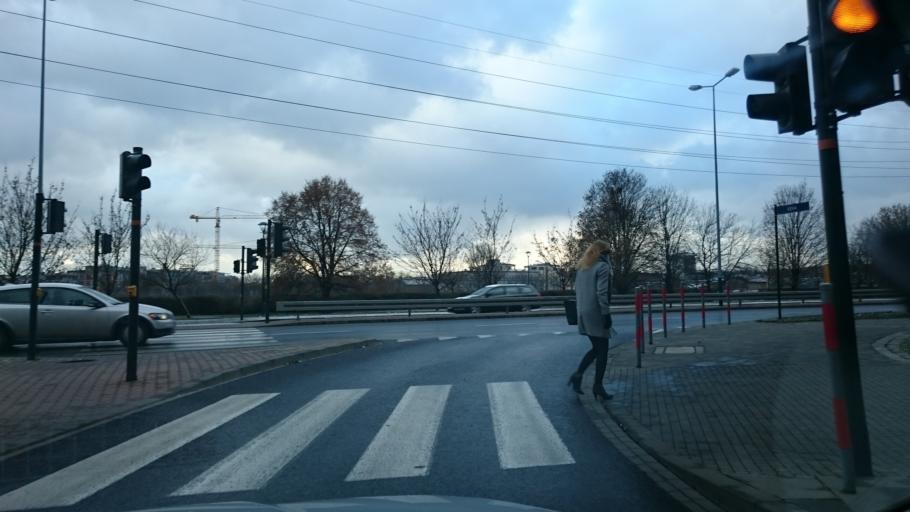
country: PL
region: Lesser Poland Voivodeship
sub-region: Krakow
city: Krakow
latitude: 50.0533
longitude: 19.9585
